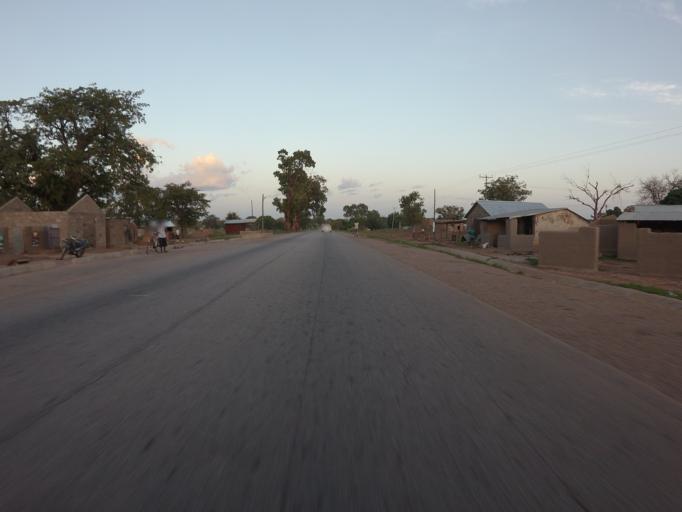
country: GH
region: Upper East
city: Navrongo
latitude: 10.8652
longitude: -1.0379
